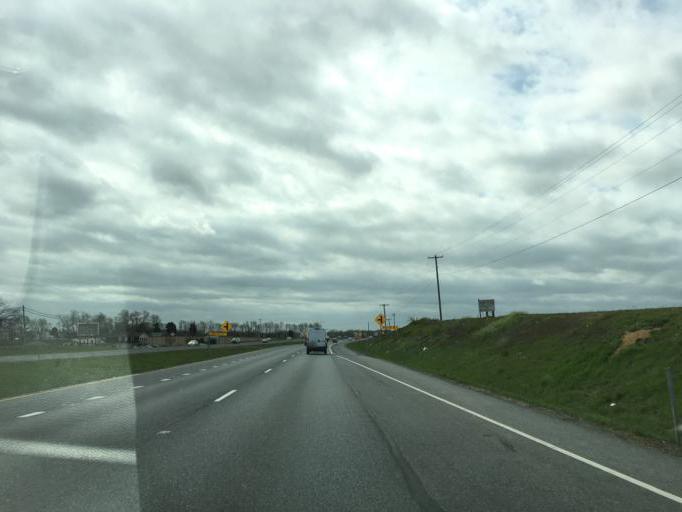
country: US
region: Maryland
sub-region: Frederick County
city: Clover Hill
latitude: 39.4847
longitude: -77.3974
